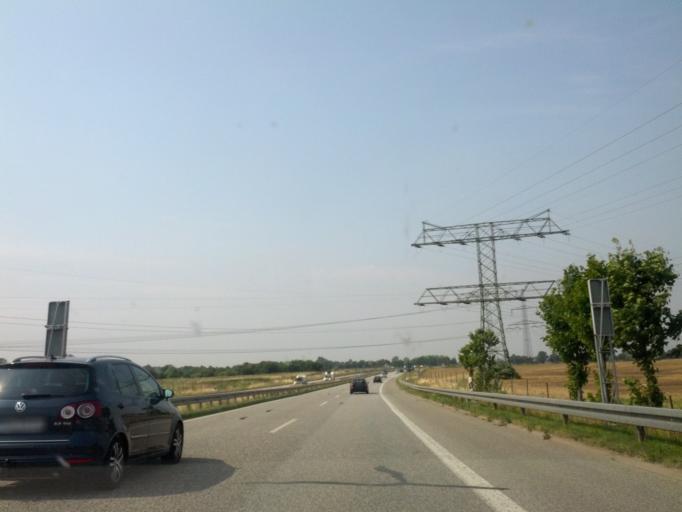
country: DE
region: Mecklenburg-Vorpommern
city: Zarrendorf
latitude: 54.2546
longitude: 13.1117
